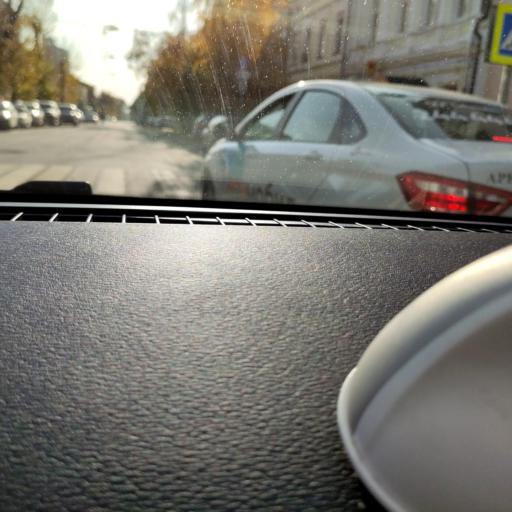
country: RU
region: Samara
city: Samara
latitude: 53.1854
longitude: 50.0952
